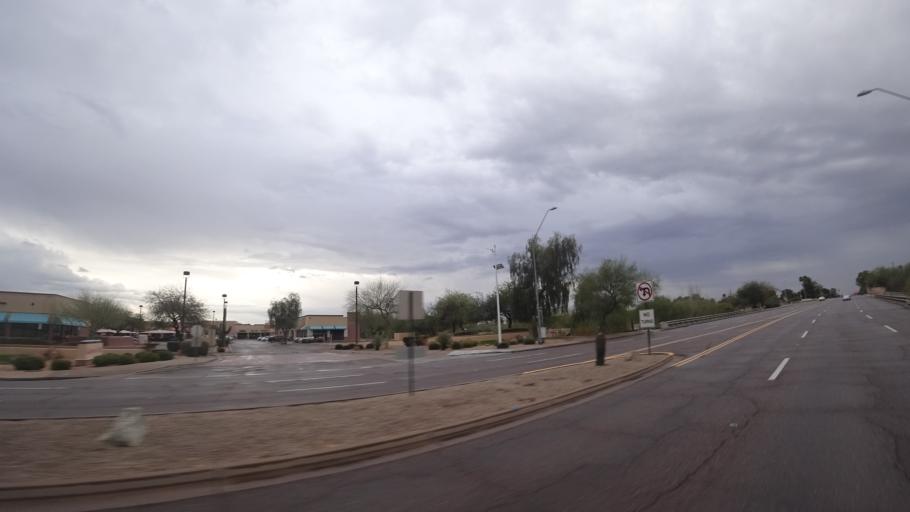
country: US
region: Arizona
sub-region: Maricopa County
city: Scottsdale
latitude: 33.5374
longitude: -111.9087
